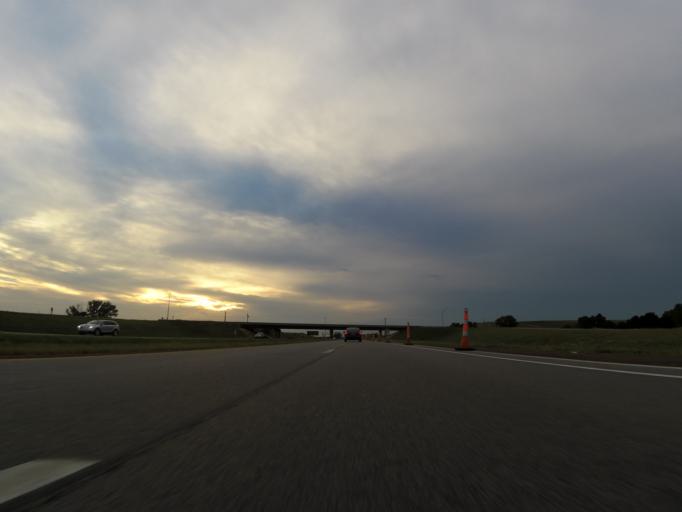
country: US
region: Kansas
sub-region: Sedgwick County
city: Valley Center
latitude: 37.7557
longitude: -97.3878
